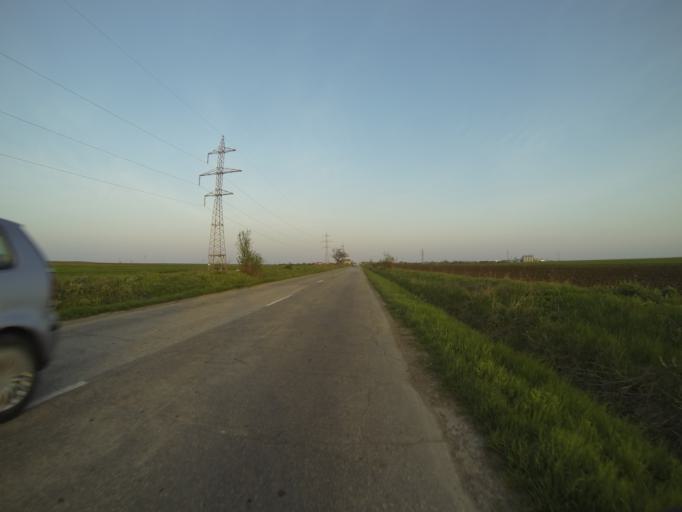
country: RO
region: Dolj
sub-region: Comuna Dranicu
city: Dranic
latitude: 44.0610
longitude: 23.8238
